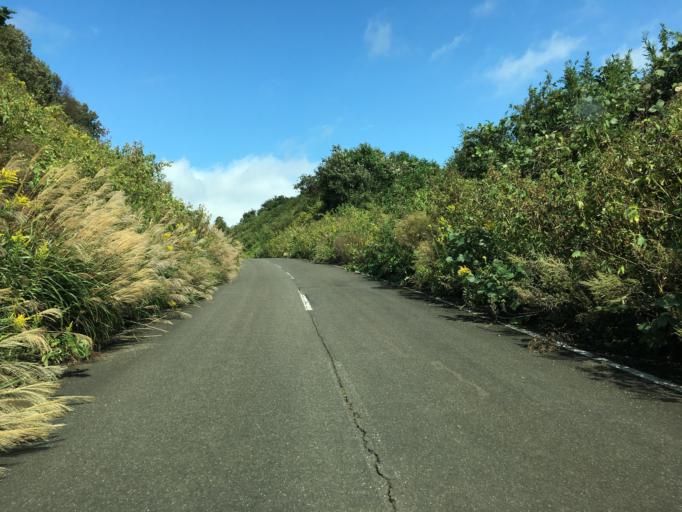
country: JP
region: Fukushima
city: Nihommatsu
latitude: 37.6541
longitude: 140.4184
